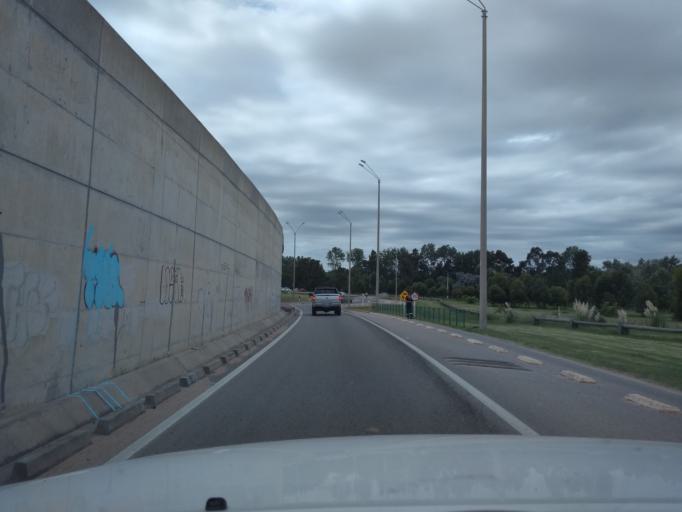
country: UY
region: Canelones
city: Barra de Carrasco
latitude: -34.8417
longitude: -56.0137
